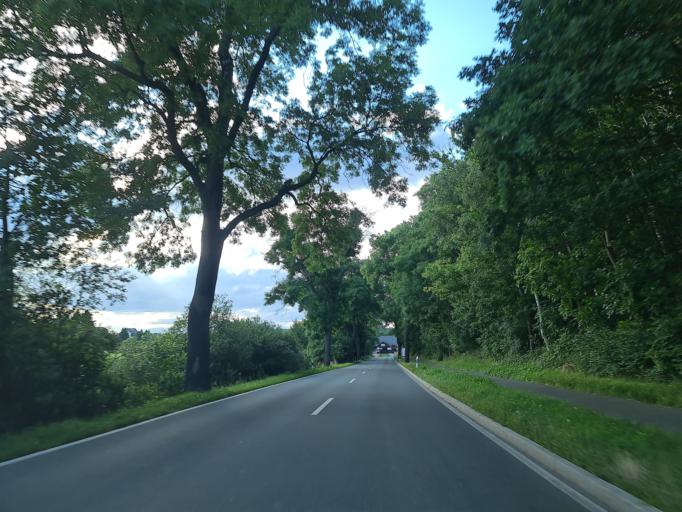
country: DE
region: Saxony
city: Pausa
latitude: 50.5736
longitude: 11.9948
